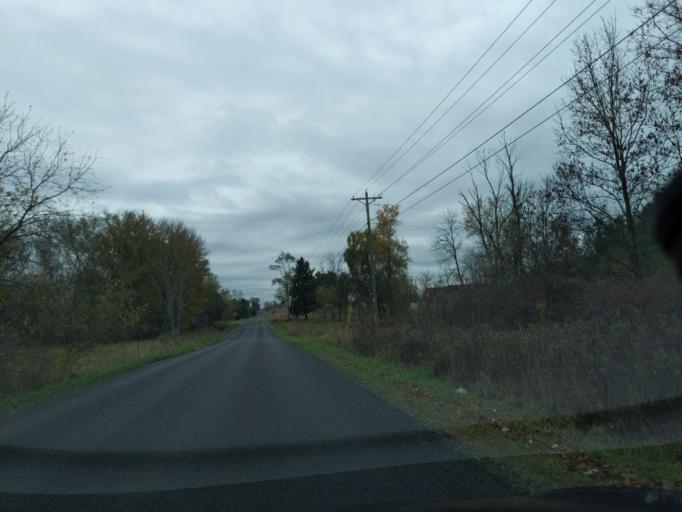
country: US
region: Michigan
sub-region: Eaton County
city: Eaton Rapids
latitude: 42.4673
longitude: -84.6008
